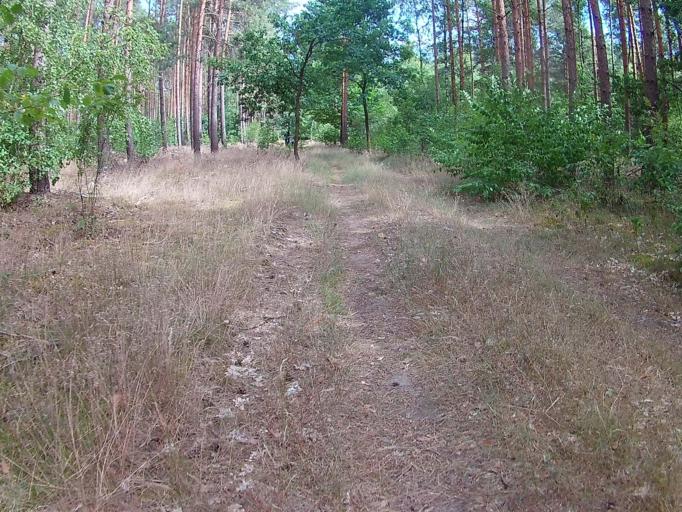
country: DE
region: Brandenburg
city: Zeuthen
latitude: 52.3982
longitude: 13.6118
